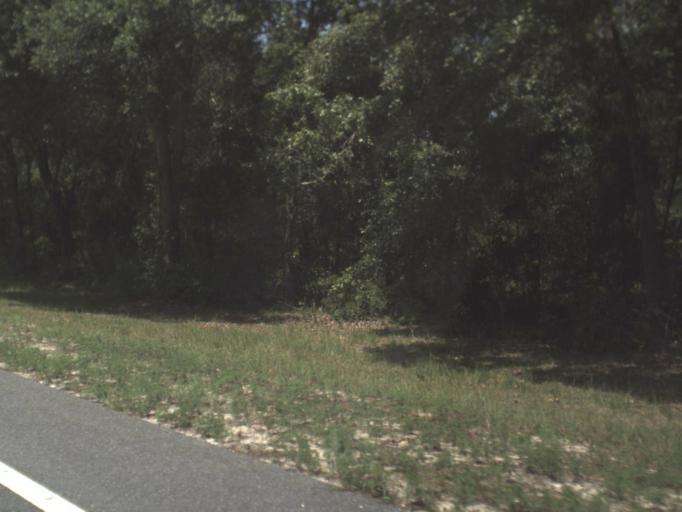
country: US
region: Florida
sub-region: Levy County
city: Williston
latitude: 29.4302
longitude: -82.4183
